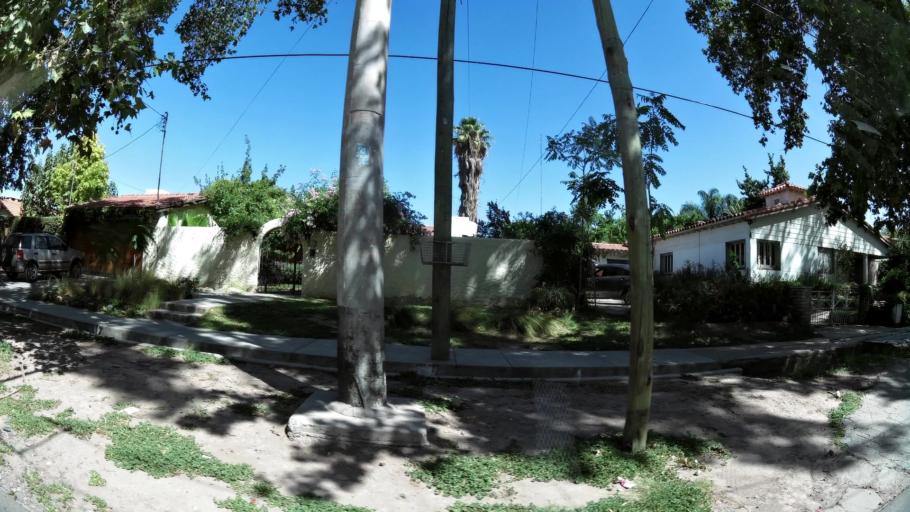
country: AR
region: Mendoza
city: Villa Nueva
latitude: -32.8927
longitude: -68.7990
